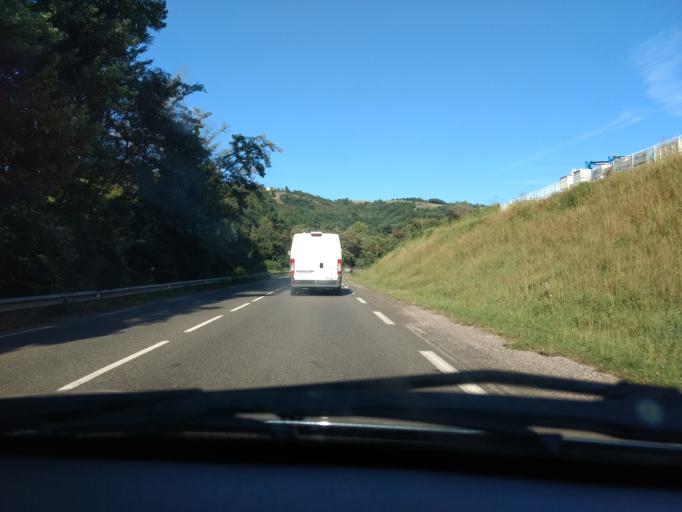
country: FR
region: Midi-Pyrenees
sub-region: Departement de l'Aveyron
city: Decazeville
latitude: 44.5586
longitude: 2.2712
